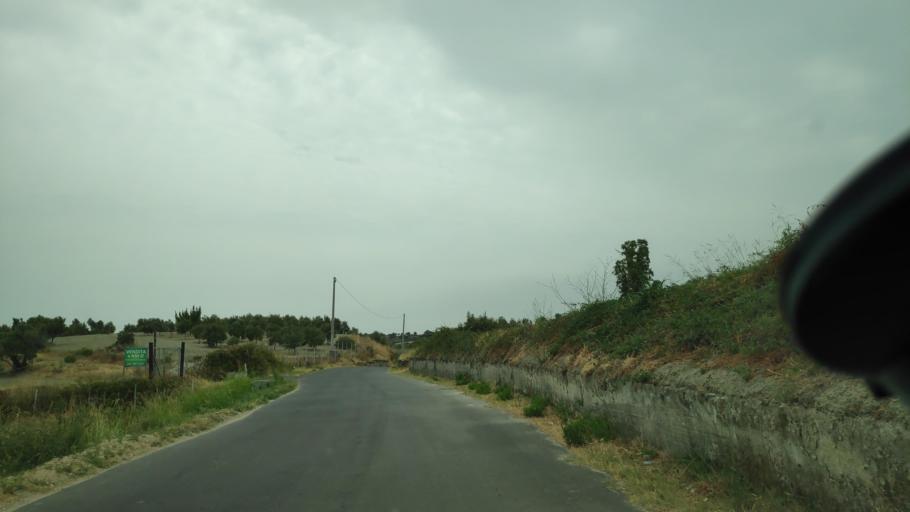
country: IT
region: Calabria
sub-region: Provincia di Catanzaro
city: Martelli-Laganosa
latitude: 38.6653
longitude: 16.5295
